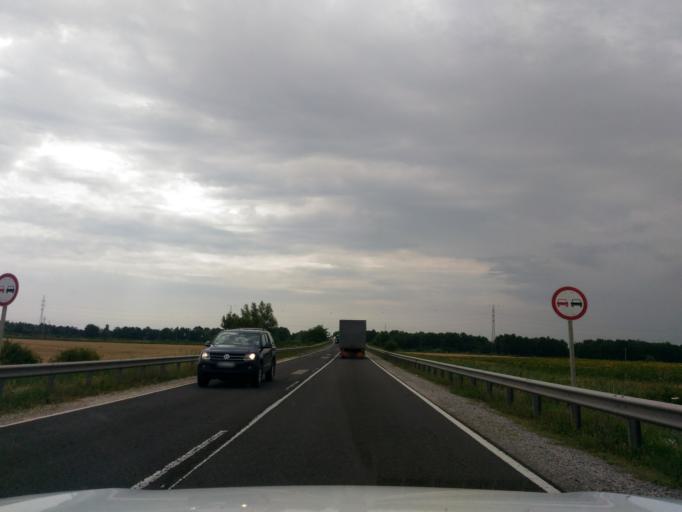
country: HU
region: Jasz-Nagykun-Szolnok
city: Toszeg
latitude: 47.1532
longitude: 20.1277
